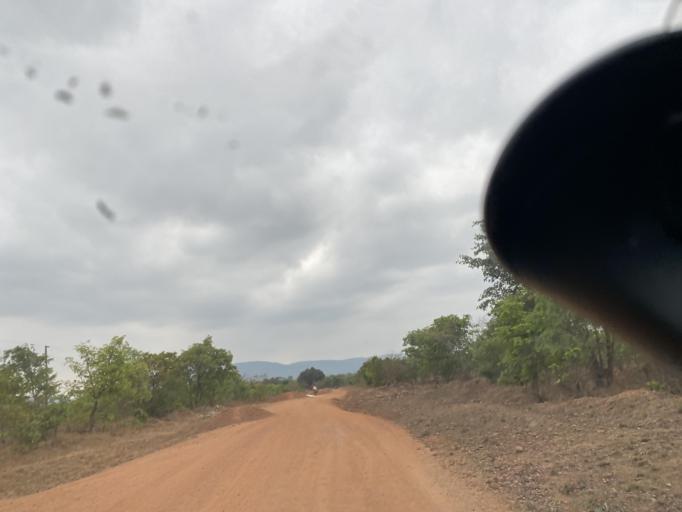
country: ZM
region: Lusaka
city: Chongwe
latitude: -15.2220
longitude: 28.7518
